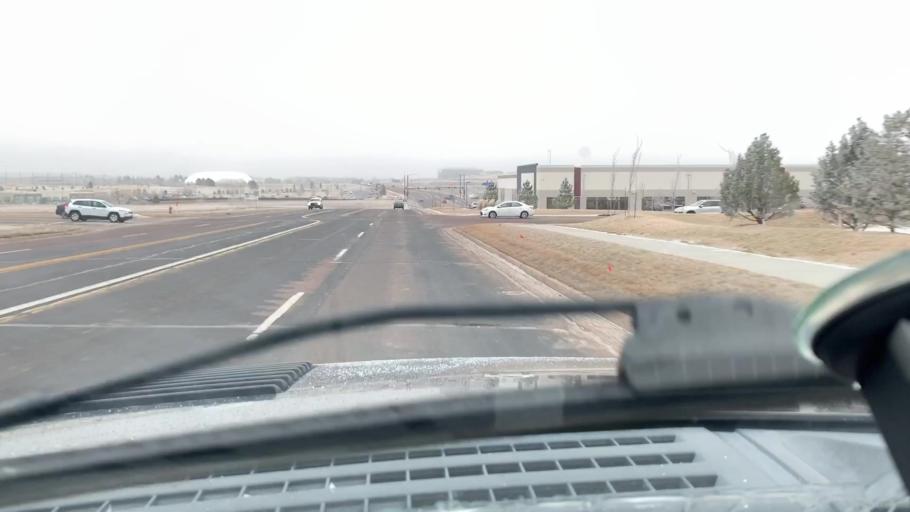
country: US
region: Colorado
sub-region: Arapahoe County
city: Centennial
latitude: 39.5877
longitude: -104.8621
